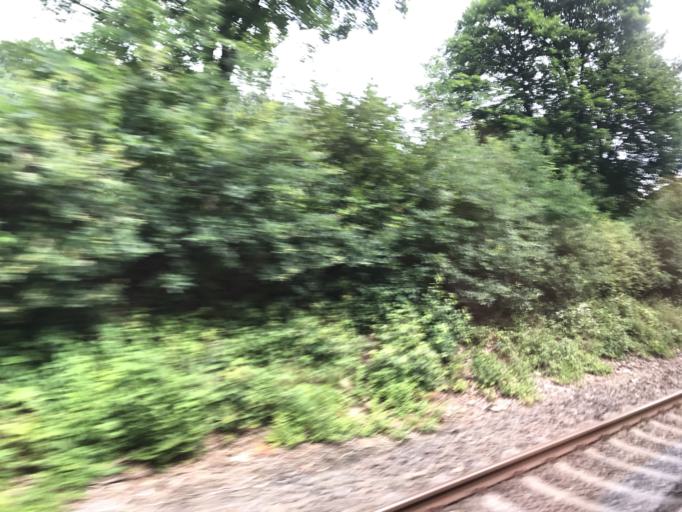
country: DE
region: Rheinland-Pfalz
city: Gutenacker
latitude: 50.3288
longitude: 7.9293
